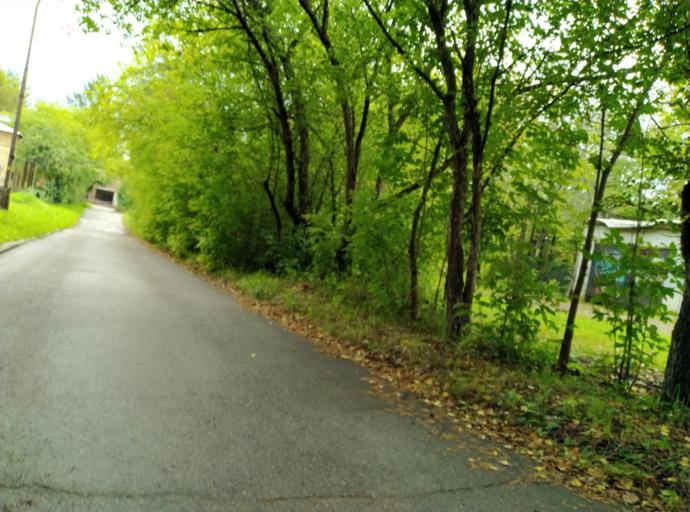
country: RU
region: Krasnoyarskiy
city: Krasnoyarsk
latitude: 55.9892
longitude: 92.7613
